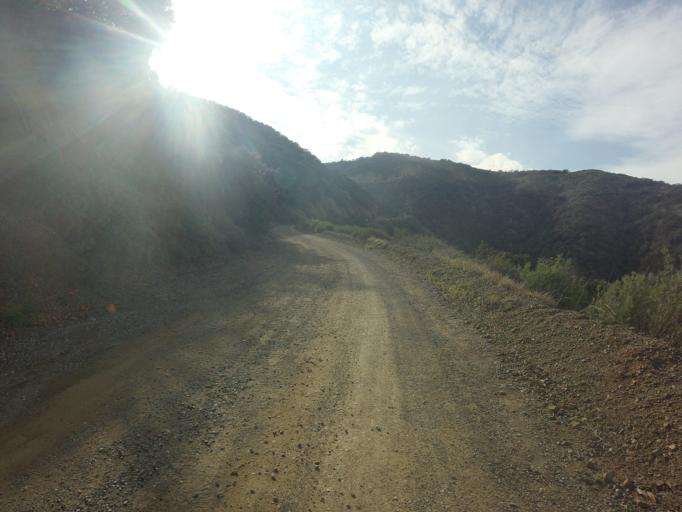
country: US
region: California
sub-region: Riverside County
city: Corona
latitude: 33.8402
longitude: -117.6223
